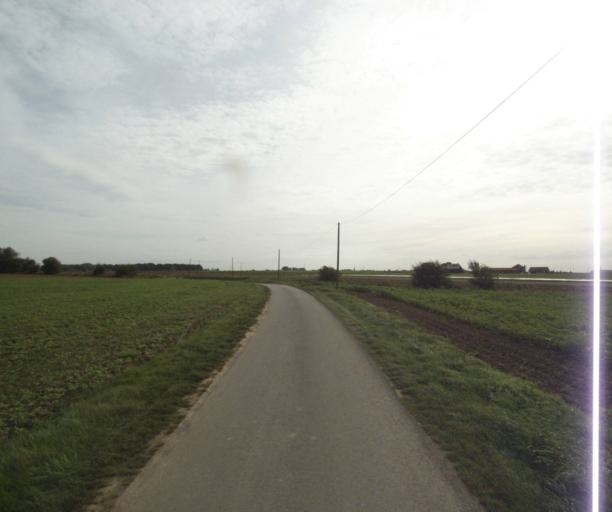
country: FR
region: Nord-Pas-de-Calais
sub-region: Departement du Nord
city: Radinghem-en-Weppes
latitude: 50.6109
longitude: 2.8915
